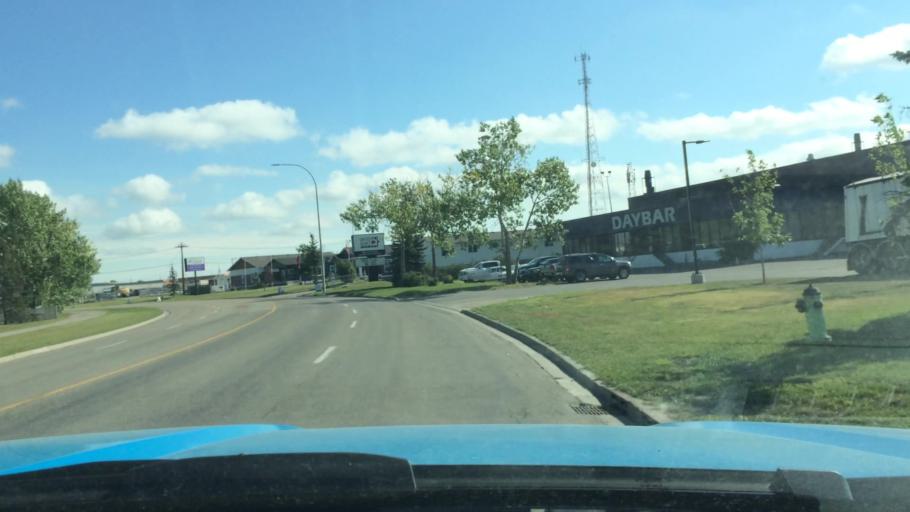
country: CA
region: Alberta
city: Airdrie
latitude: 51.2911
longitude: -113.9908
